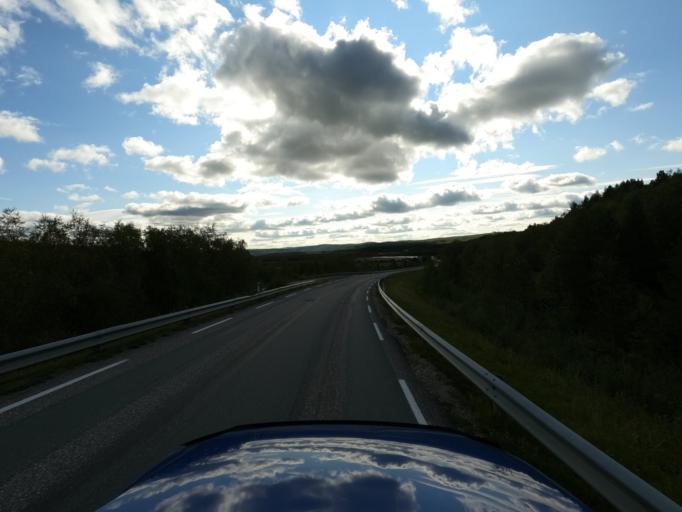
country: NO
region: Finnmark Fylke
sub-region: Karasjok
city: Karasjohka
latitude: 69.4284
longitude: 25.7942
